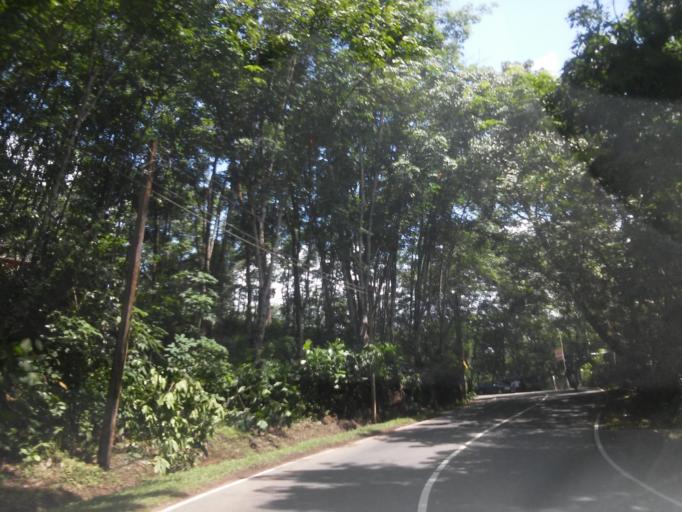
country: LK
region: Sabaragamuwa
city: Ratnapura
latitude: 6.7264
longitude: 80.3254
